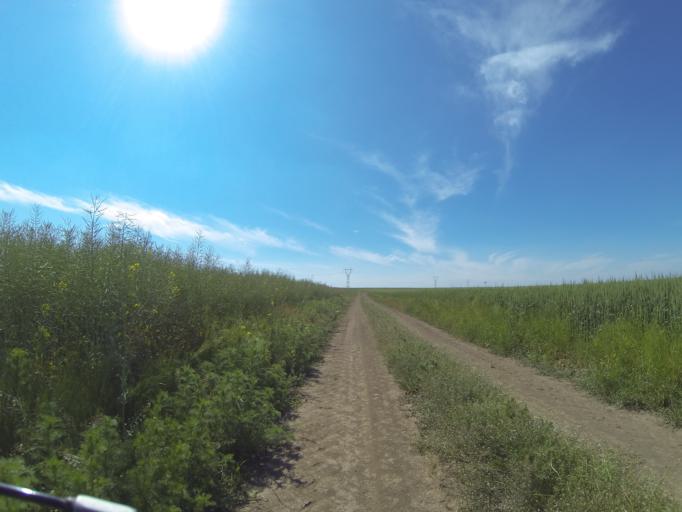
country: RO
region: Dolj
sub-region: Comuna Cosoveni
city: Cosoveni
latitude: 44.2569
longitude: 24.0067
